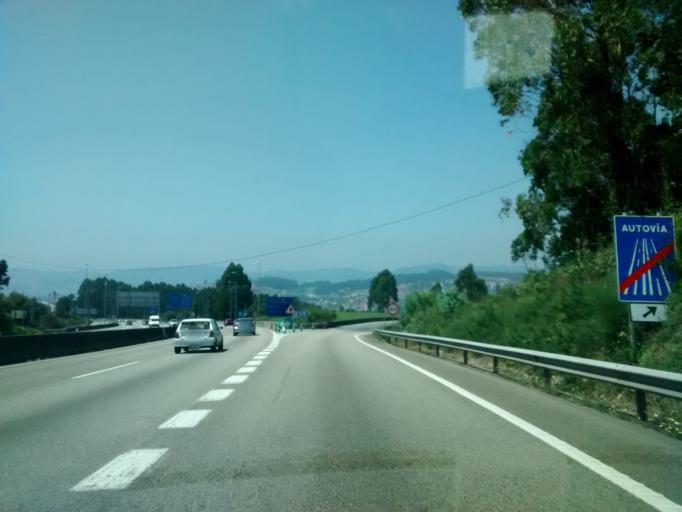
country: ES
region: Galicia
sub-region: Provincia de Pontevedra
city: Porrino
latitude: 42.2092
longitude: -8.6597
